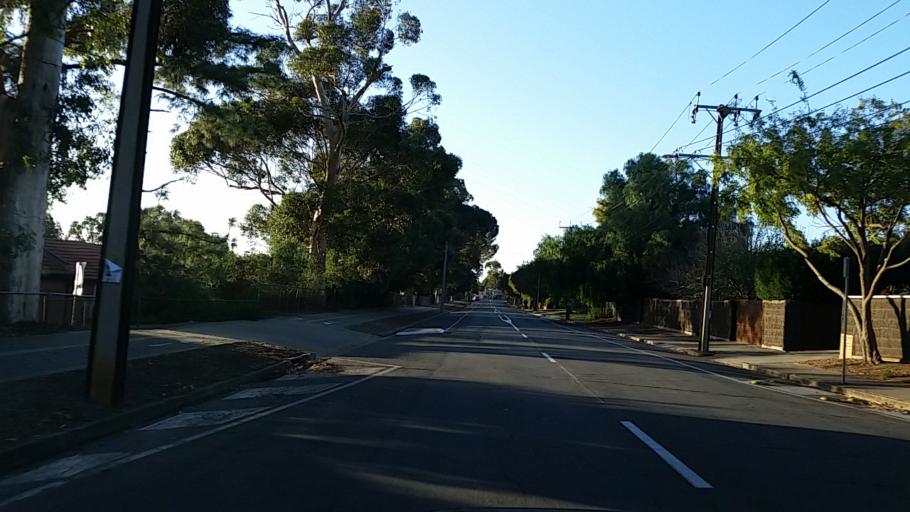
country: AU
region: South Australia
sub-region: Burnside
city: Glenunga
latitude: -34.9668
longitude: 138.6357
